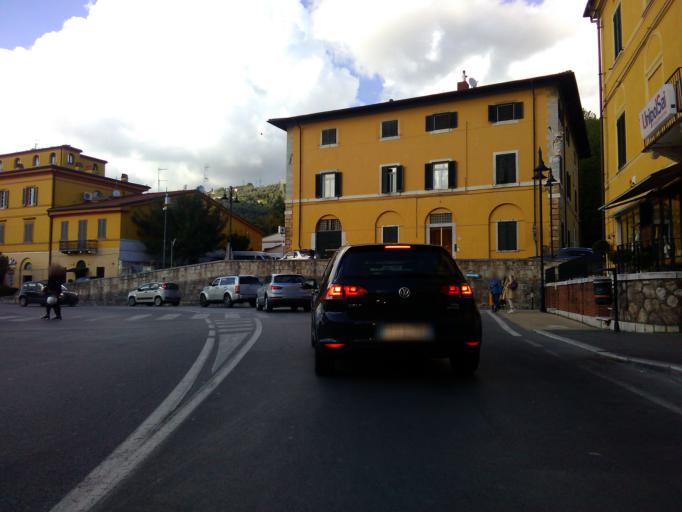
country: IT
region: Tuscany
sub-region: Provincia di Lucca
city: Pietrasanta
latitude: 43.9594
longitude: 10.2284
